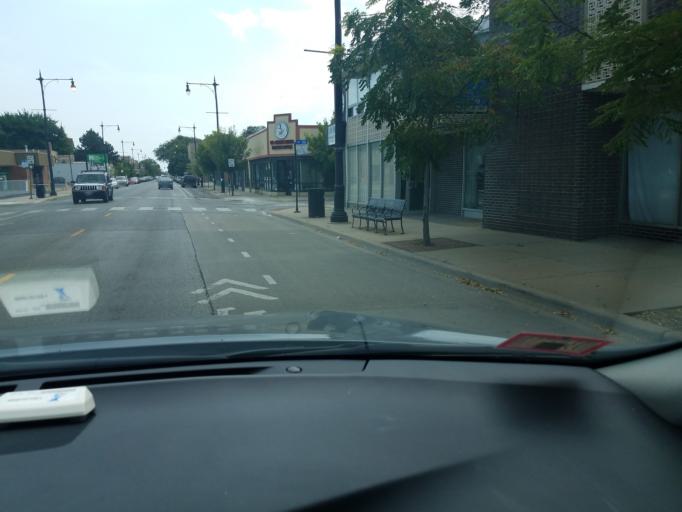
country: US
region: Illinois
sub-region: Cook County
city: Harwood Heights
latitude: 41.9669
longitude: -87.7600
